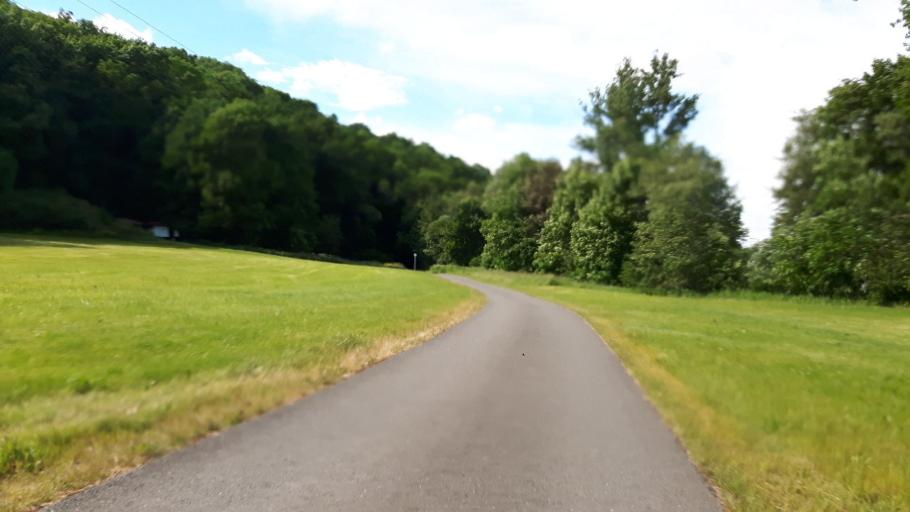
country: DE
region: Thuringia
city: Barchfeld
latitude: 50.8215
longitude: 11.1792
